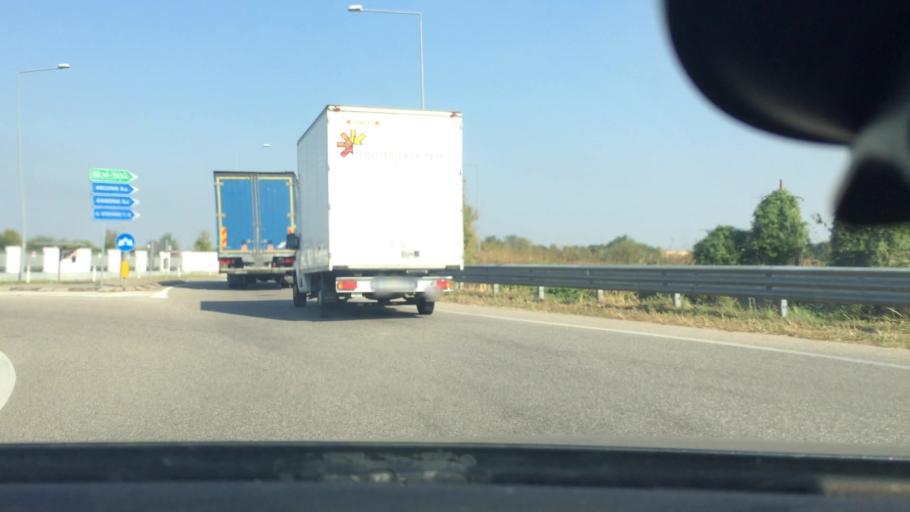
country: IT
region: Lombardy
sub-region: Citta metropolitana di Milano
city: Marcallo
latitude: 45.4878
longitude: 8.8812
